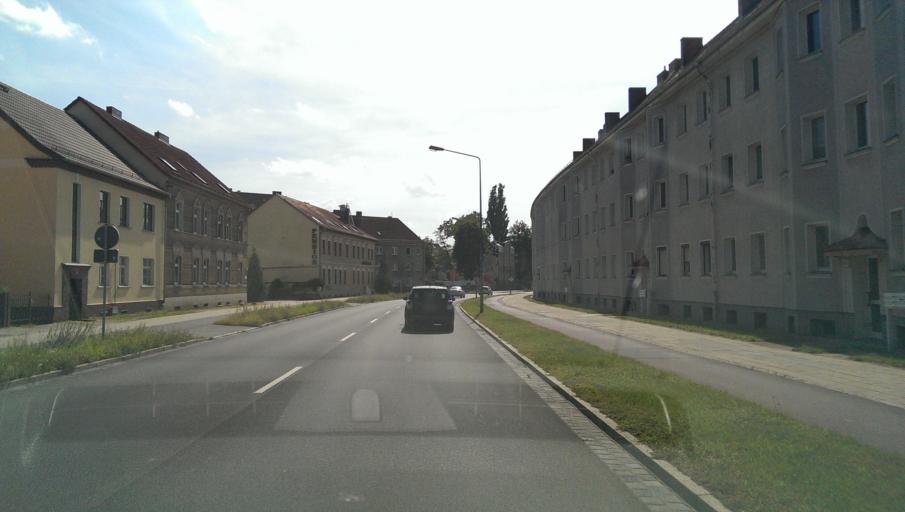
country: DE
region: Saxony-Anhalt
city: Wittenburg
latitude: 51.8738
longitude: 12.6477
